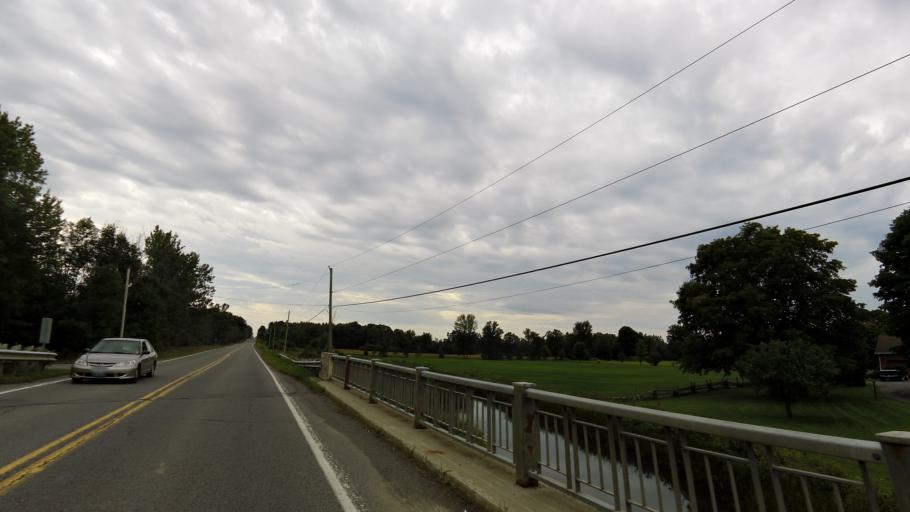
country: CA
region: Ontario
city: Ottawa
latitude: 45.2198
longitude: -75.4645
